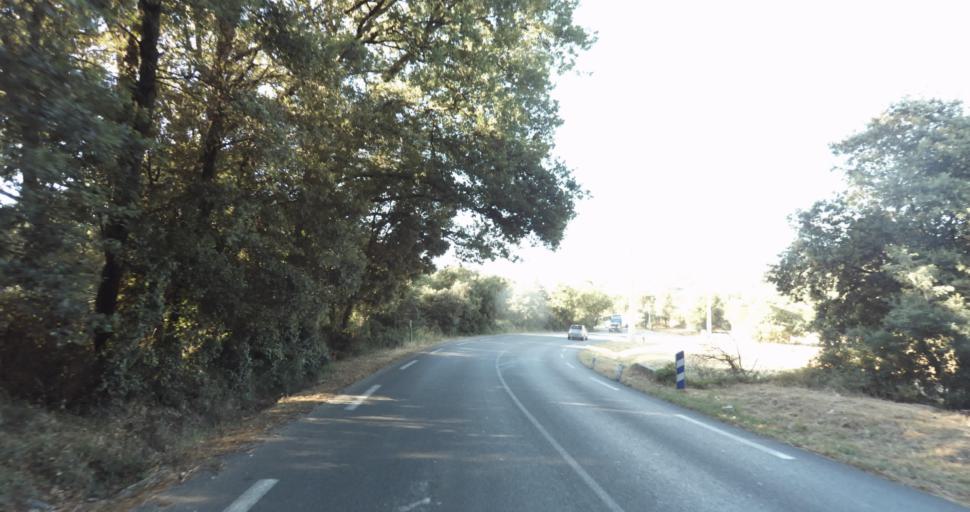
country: FR
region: Provence-Alpes-Cote d'Azur
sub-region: Departement du Var
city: La Croix-Valmer
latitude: 43.2206
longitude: 6.5703
